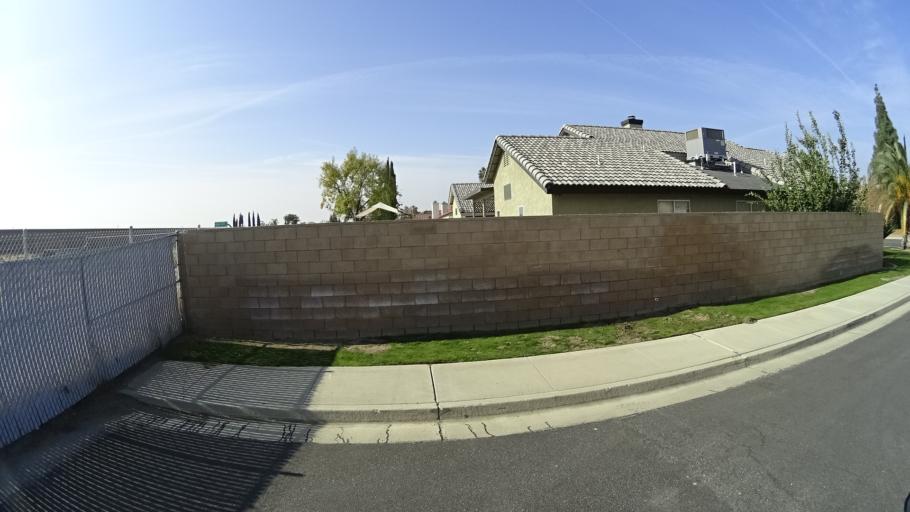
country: US
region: California
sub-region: Kern County
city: Greenacres
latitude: 35.3628
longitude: -119.0993
